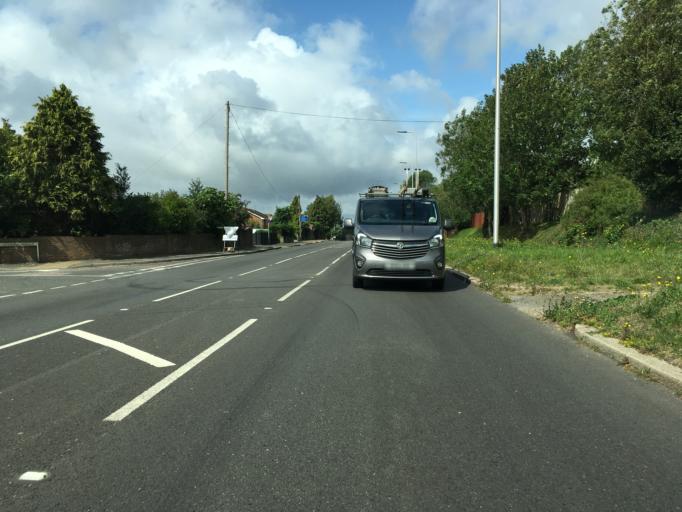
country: GB
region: England
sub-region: West Sussex
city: Findon
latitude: 50.8410
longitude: -0.4146
